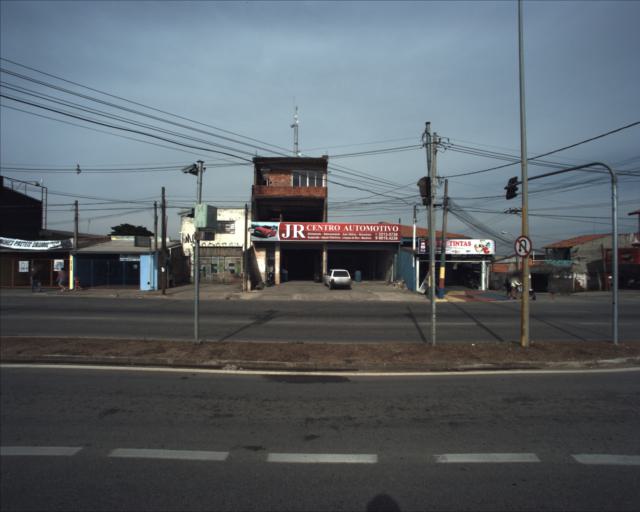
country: BR
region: Sao Paulo
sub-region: Sorocaba
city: Sorocaba
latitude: -23.4528
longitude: -47.5103
